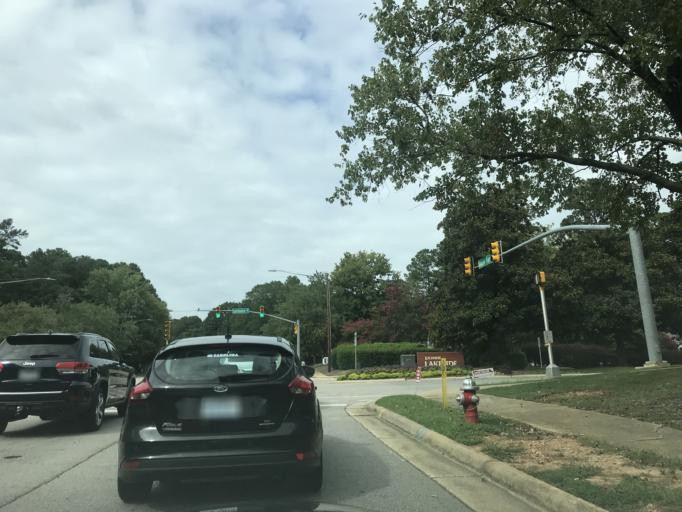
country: US
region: North Carolina
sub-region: Wake County
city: Cary
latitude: 35.7290
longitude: -78.7772
